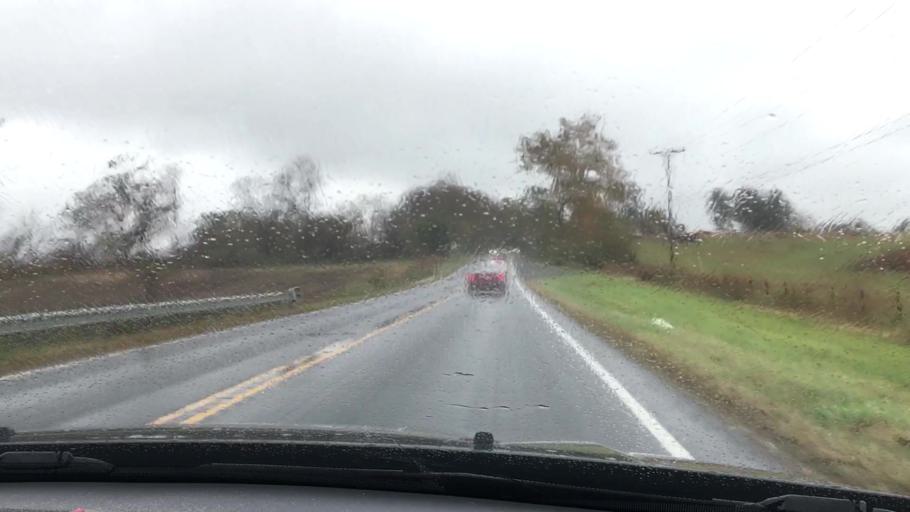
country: US
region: Virginia
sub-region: Loudoun County
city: Leesburg
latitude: 39.1843
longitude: -77.5351
